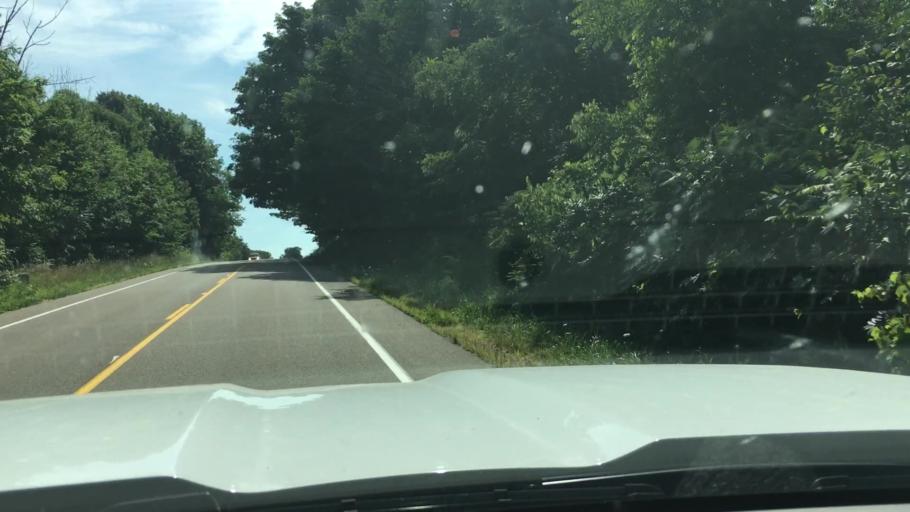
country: US
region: Michigan
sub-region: Kent County
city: Lowell
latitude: 42.8856
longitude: -85.3619
